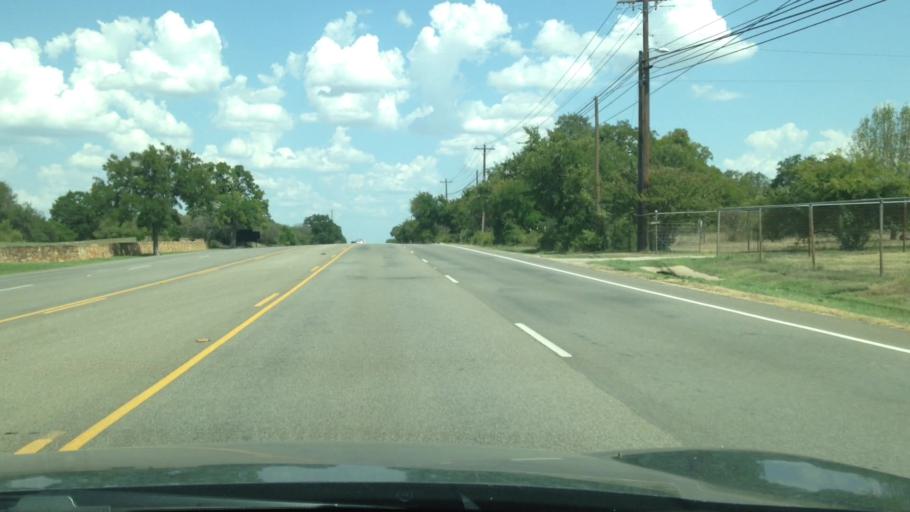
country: US
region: Texas
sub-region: Williamson County
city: Leander
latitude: 30.6359
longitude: -97.7891
